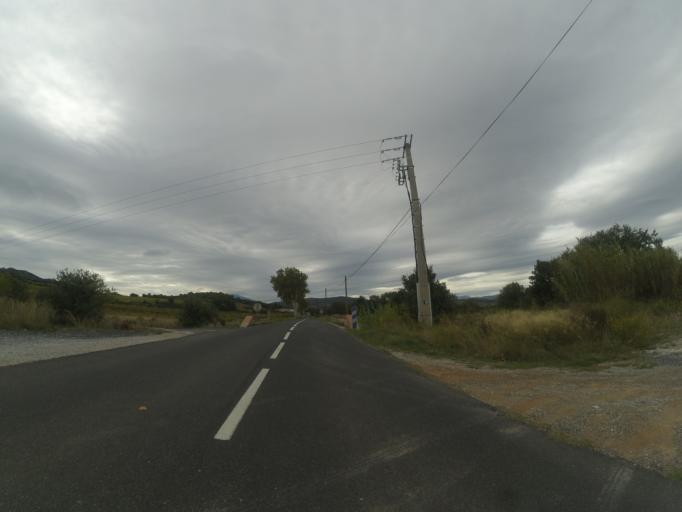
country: FR
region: Languedoc-Roussillon
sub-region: Departement des Pyrenees-Orientales
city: Estagel
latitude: 42.7674
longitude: 2.6922
